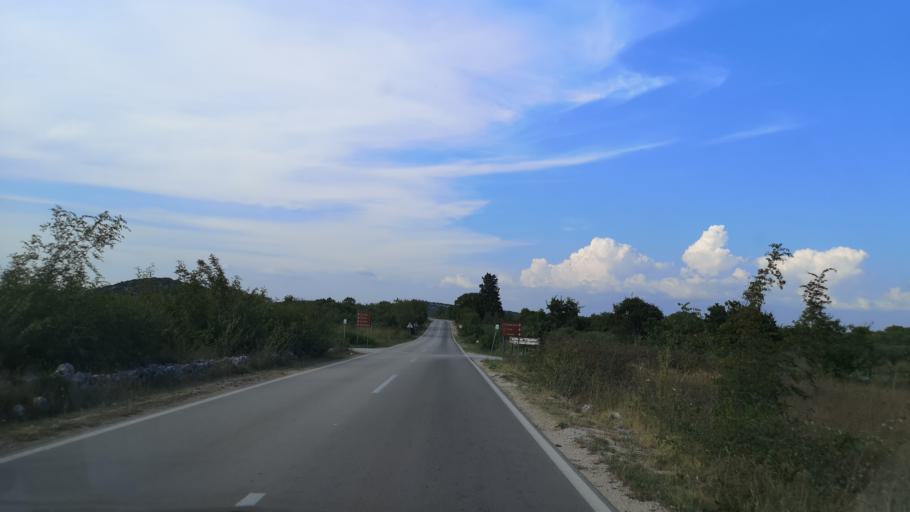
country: HR
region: Sibensko-Kniniska
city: Vodice
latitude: 43.8078
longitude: 15.7760
